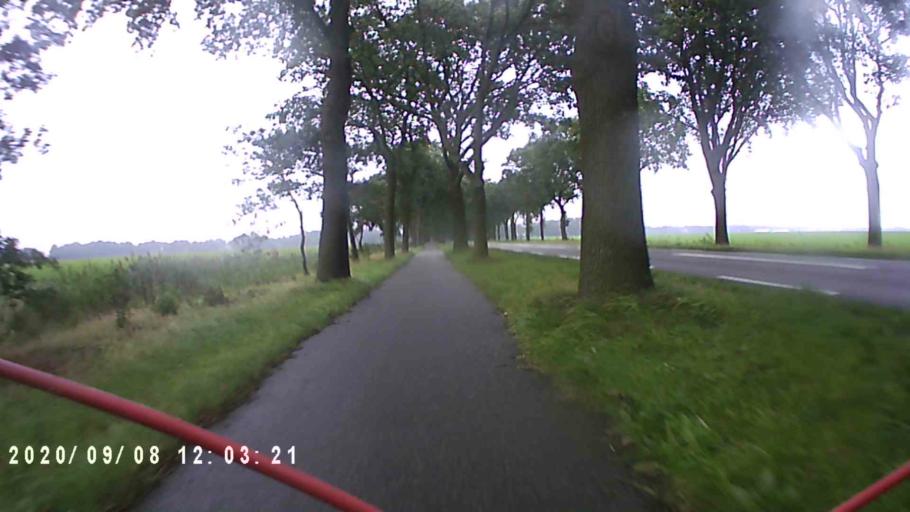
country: NL
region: Groningen
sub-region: Gemeente Hoogezand-Sappemeer
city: Sappemeer
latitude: 53.1093
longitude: 6.8131
